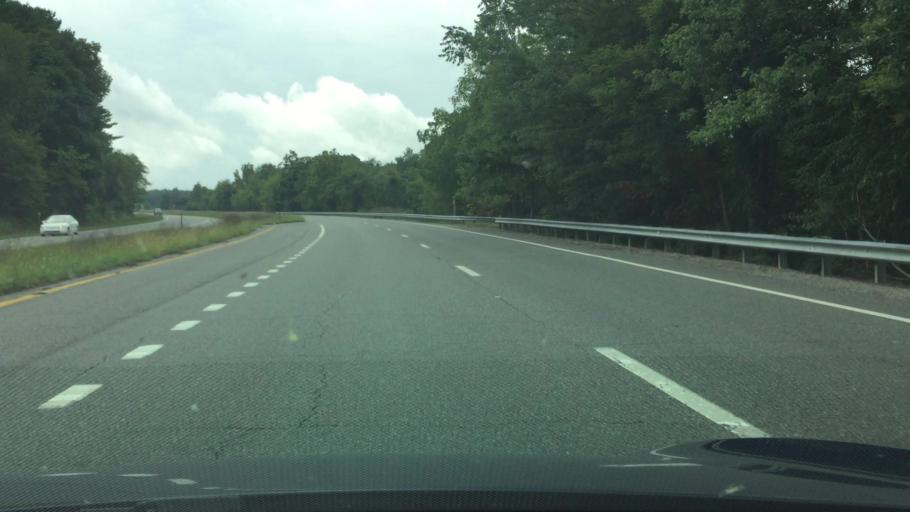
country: US
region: Virginia
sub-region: City of Radford
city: Radford
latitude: 37.1072
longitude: -80.5207
